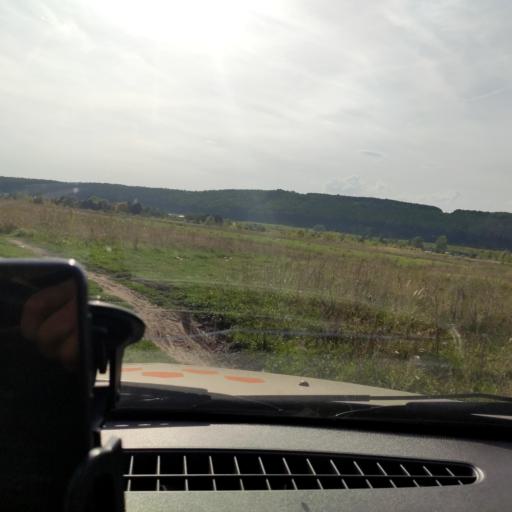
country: RU
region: Bashkortostan
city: Ufa
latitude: 54.8246
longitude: 56.1624
